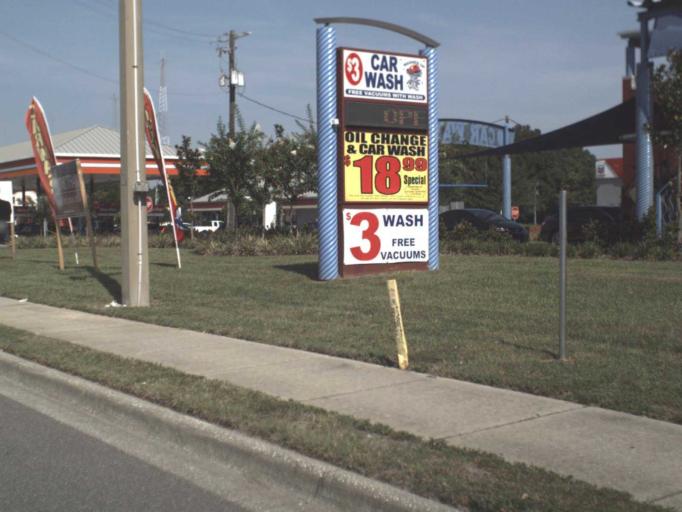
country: US
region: Florida
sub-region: Hillsborough County
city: Brandon
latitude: 27.9379
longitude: -82.2720
